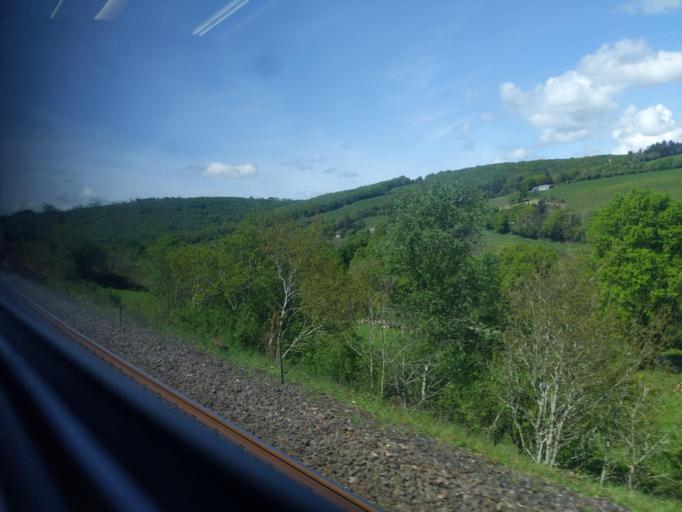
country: GB
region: England
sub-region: Cornwall
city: Lostwithiel
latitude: 50.4561
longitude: -4.6066
